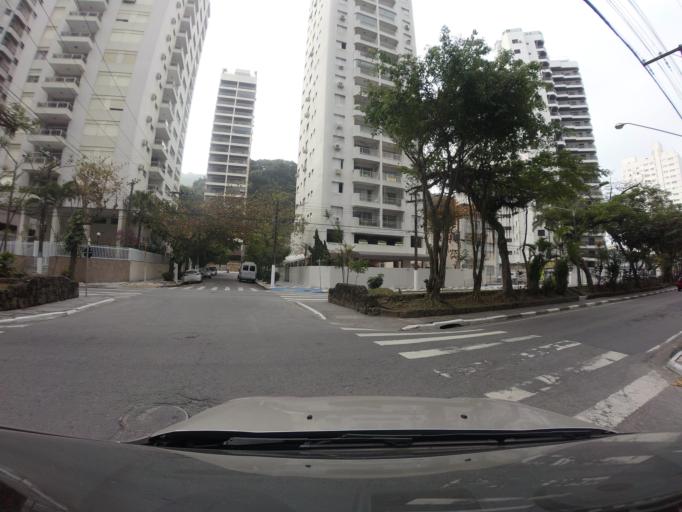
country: BR
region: Sao Paulo
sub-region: Guaruja
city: Guaruja
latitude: -23.9975
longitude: -46.2619
